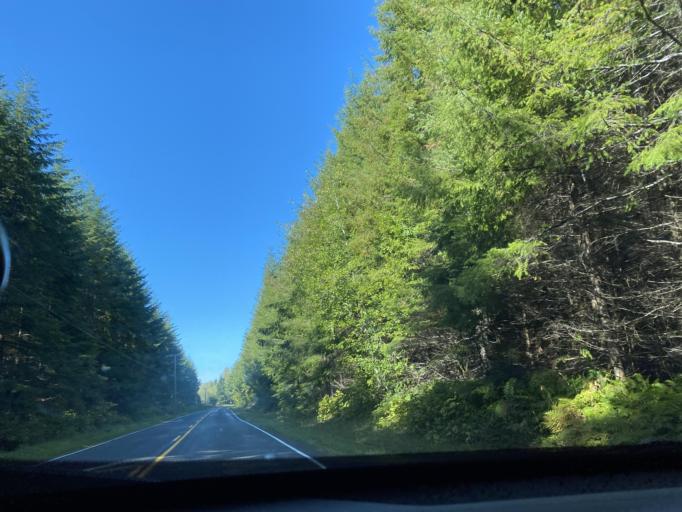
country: US
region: Washington
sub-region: Clallam County
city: Forks
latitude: 47.9470
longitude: -124.4939
